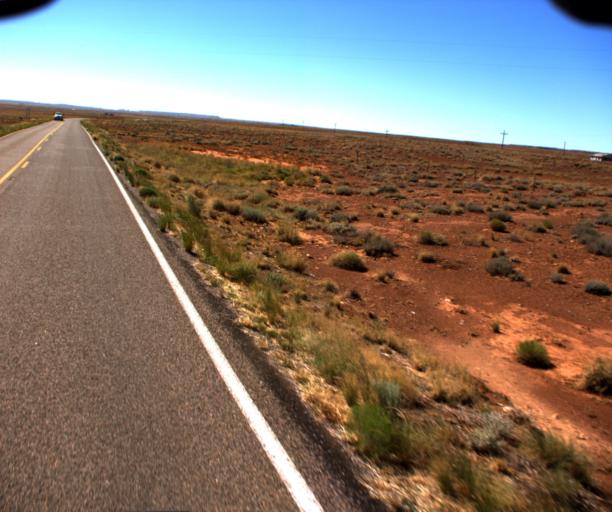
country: US
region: Arizona
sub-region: Coconino County
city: LeChee
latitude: 35.1886
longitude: -110.9367
